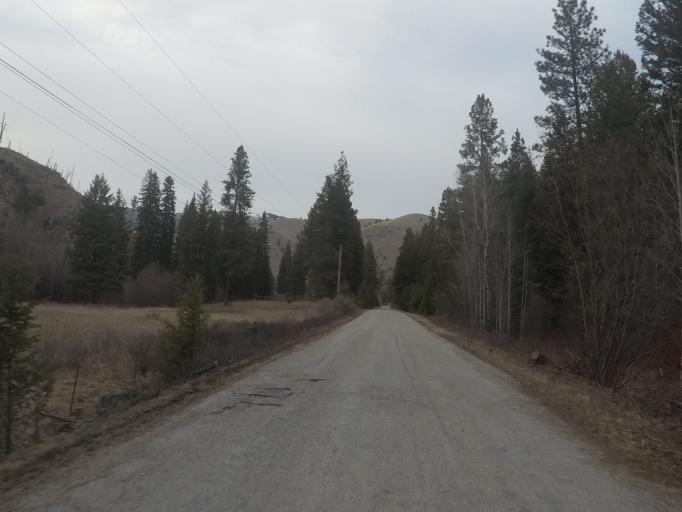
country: US
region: Montana
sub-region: Ravalli County
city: Hamilton
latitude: 45.8495
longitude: -114.0332
